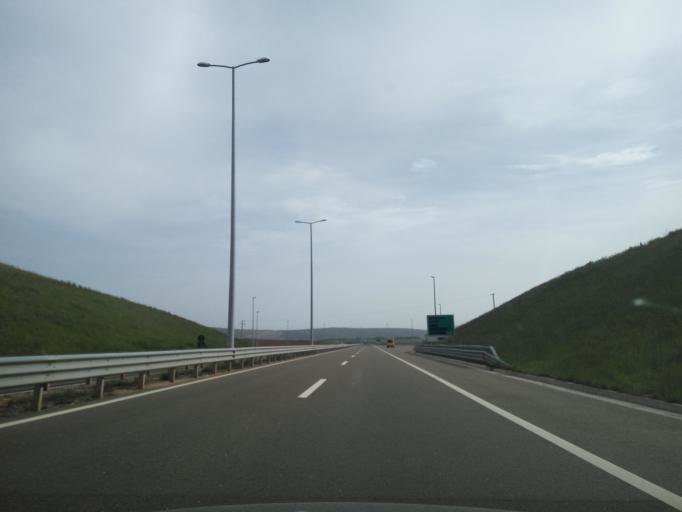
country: XK
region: Prizren
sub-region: Komuna e Malisheves
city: Malisevo
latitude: 42.4967
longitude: 20.7958
